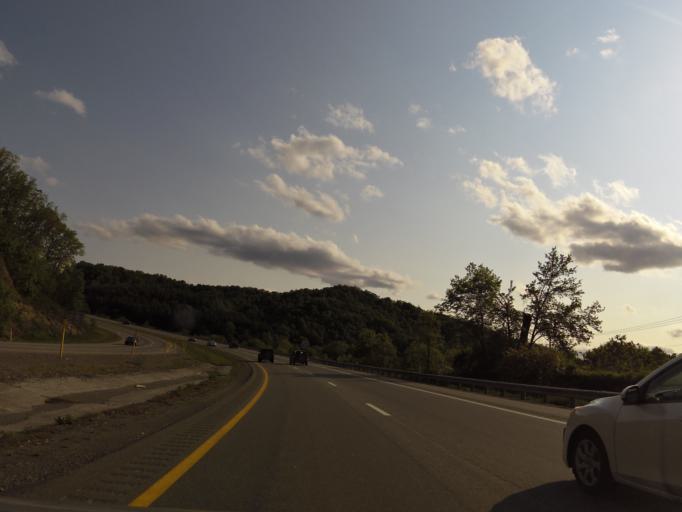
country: US
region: West Virginia
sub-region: Mercer County
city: Princeton
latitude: 37.3416
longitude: -81.1281
